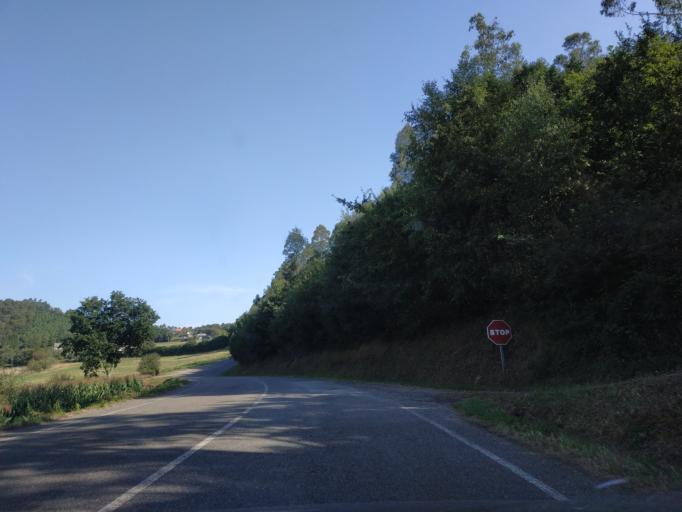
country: ES
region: Galicia
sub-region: Provincia da Coruna
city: Laracha
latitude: 43.2275
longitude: -8.5501
